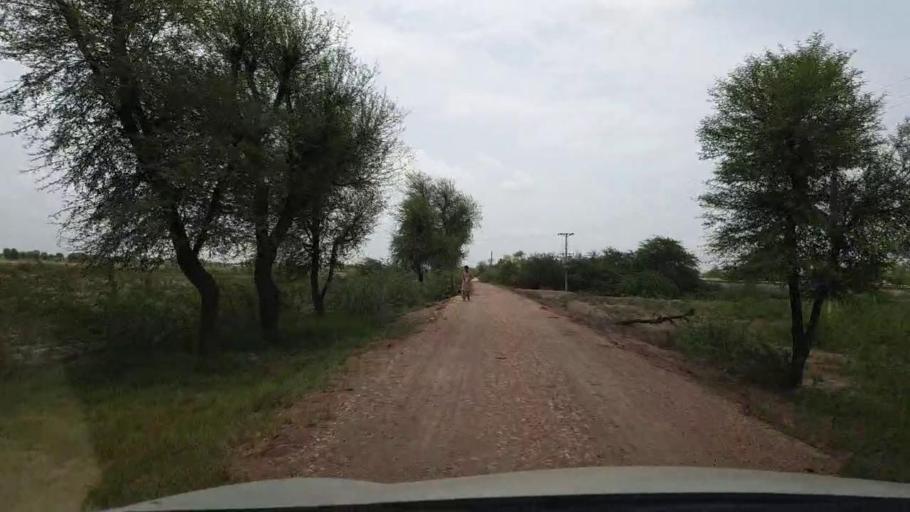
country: PK
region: Sindh
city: Chambar
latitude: 25.2127
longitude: 68.7616
